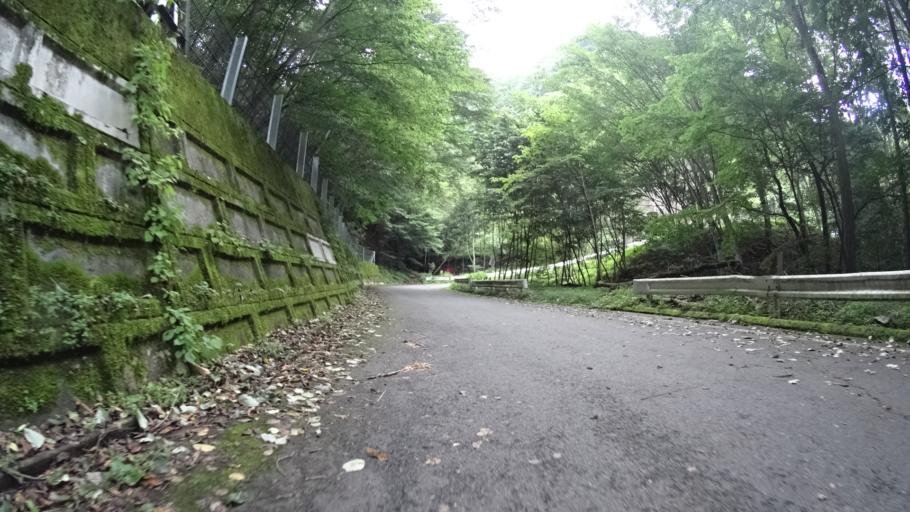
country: JP
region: Nagano
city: Saku
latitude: 36.0667
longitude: 138.6691
